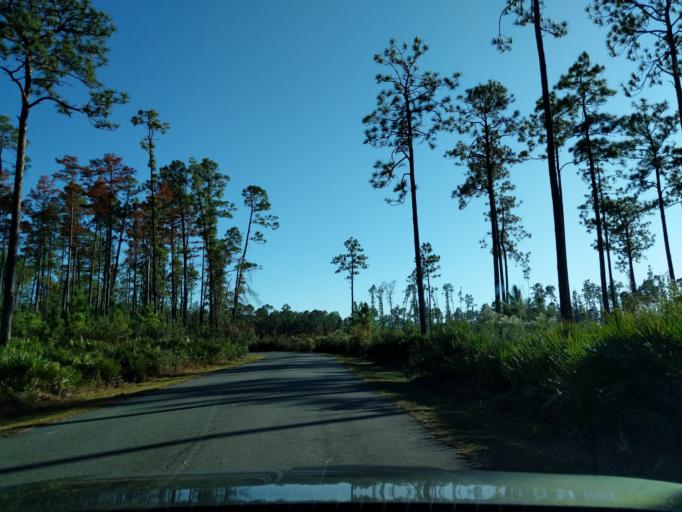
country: US
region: Georgia
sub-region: Charlton County
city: Folkston
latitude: 30.7233
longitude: -82.1399
